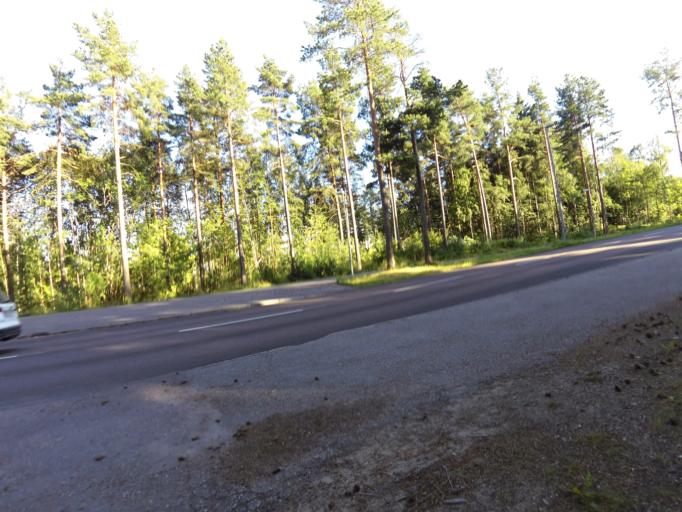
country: SE
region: Gaevleborg
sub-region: Gavle Kommun
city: Gavle
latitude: 60.6465
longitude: 17.1431
